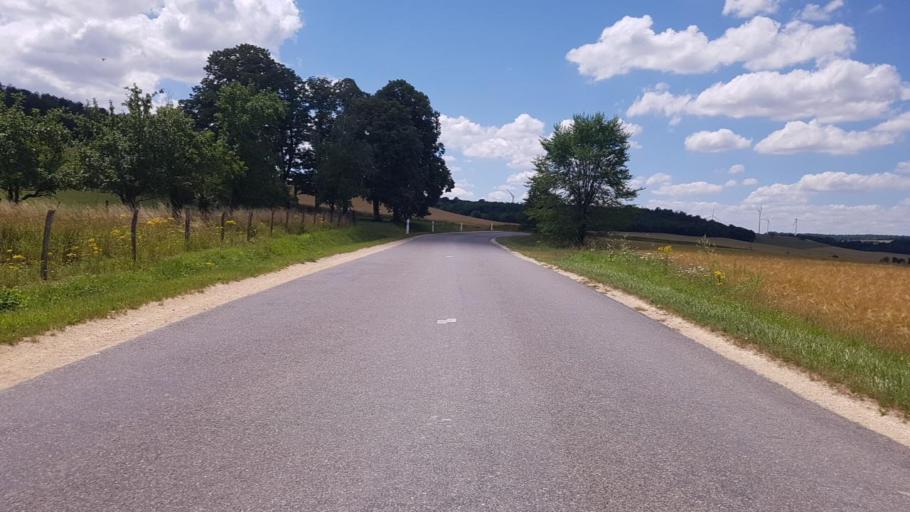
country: FR
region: Lorraine
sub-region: Departement de la Meuse
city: Vacon
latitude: 48.6406
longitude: 5.5091
